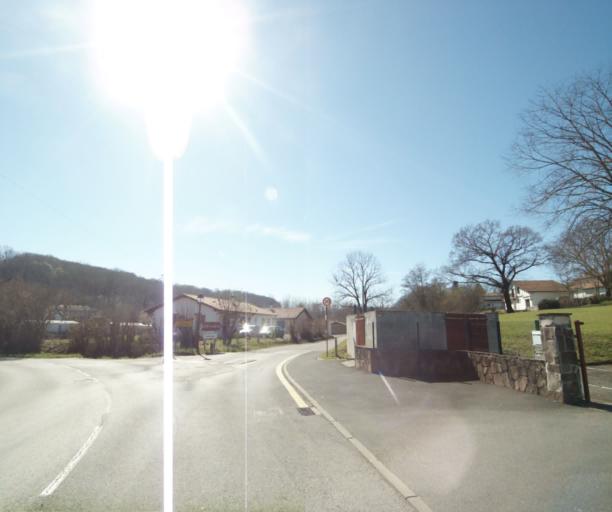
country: FR
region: Aquitaine
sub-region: Departement des Pyrenees-Atlantiques
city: Ciboure
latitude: 43.3832
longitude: -1.6951
